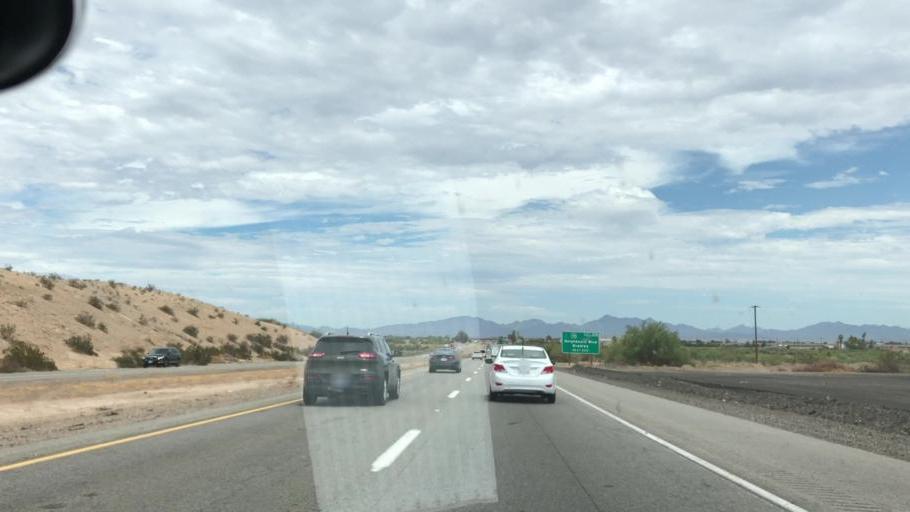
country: US
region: California
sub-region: Riverside County
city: Mesa Verde
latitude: 33.6065
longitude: -114.6724
